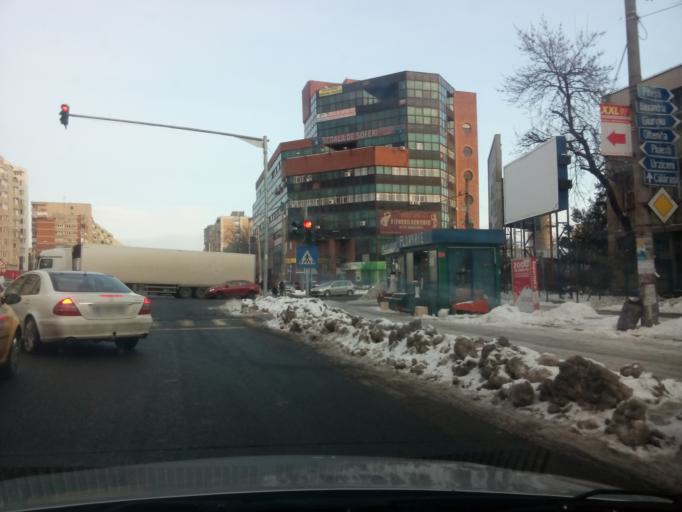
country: RO
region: Ilfov
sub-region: Comuna Fundeni-Dobroesti
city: Fundeni
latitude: 44.4425
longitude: 26.1652
